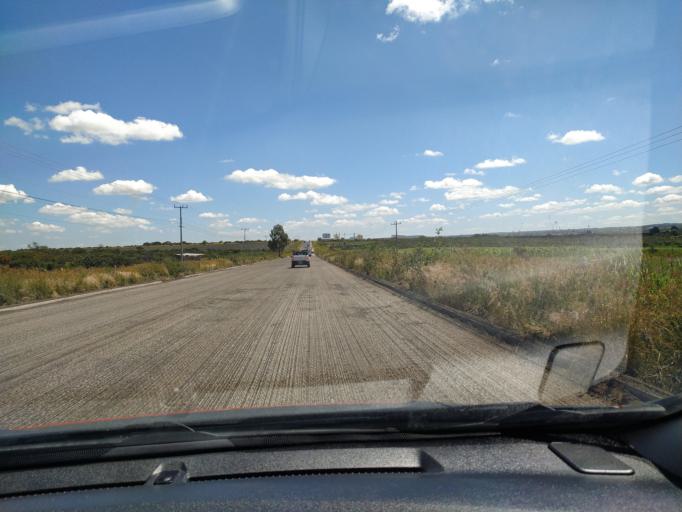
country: MX
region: Jalisco
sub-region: San Julian
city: Colonia Veintitres de Mayo
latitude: 21.0103
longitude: -102.2314
